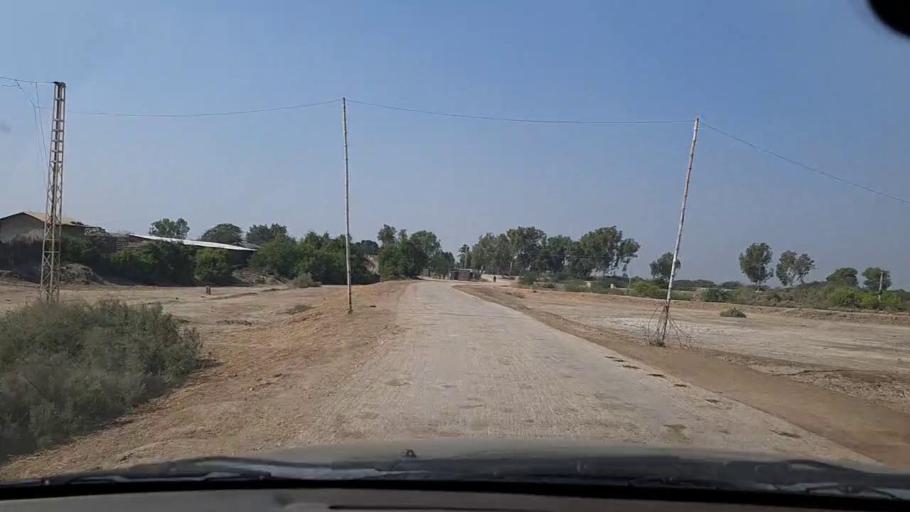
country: PK
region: Sindh
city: Chuhar Jamali
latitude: 24.4232
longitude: 67.8199
